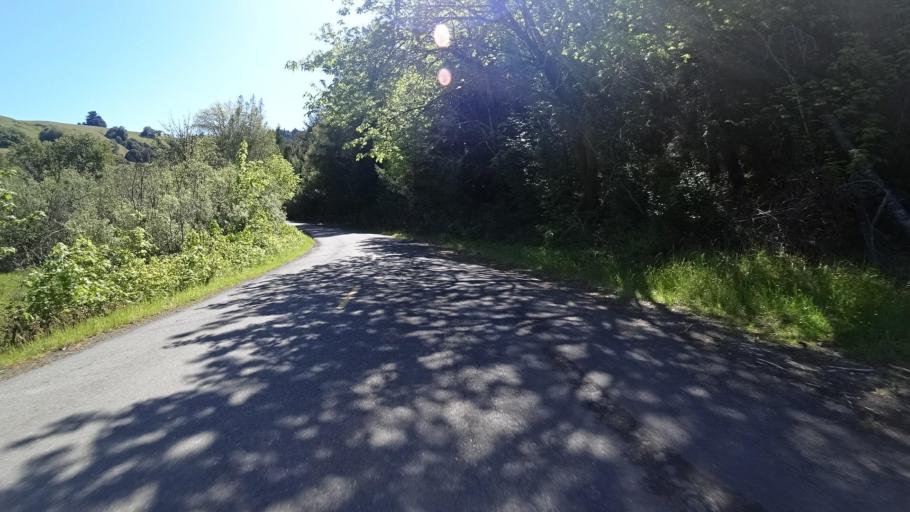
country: US
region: California
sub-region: Humboldt County
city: Rio Dell
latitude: 40.2316
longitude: -124.1162
